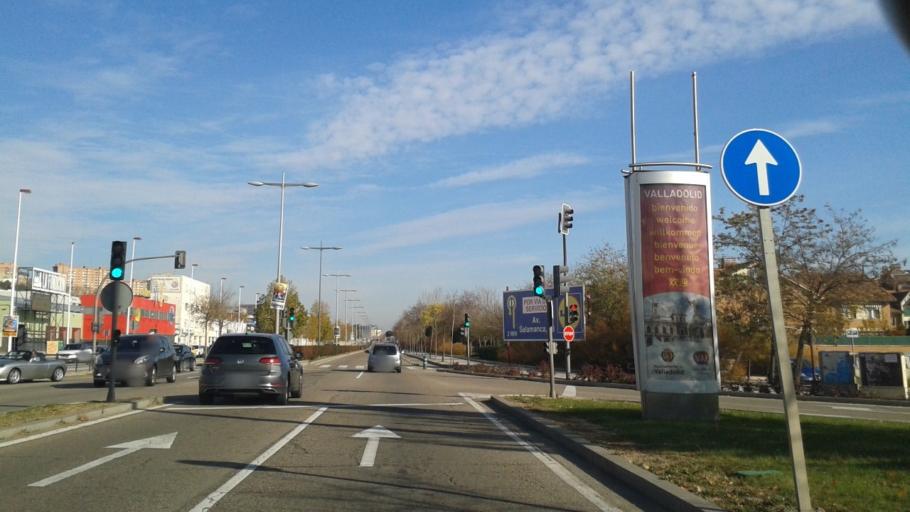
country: ES
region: Castille and Leon
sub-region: Provincia de Valladolid
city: Arroyo
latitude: 41.6250
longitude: -4.7661
